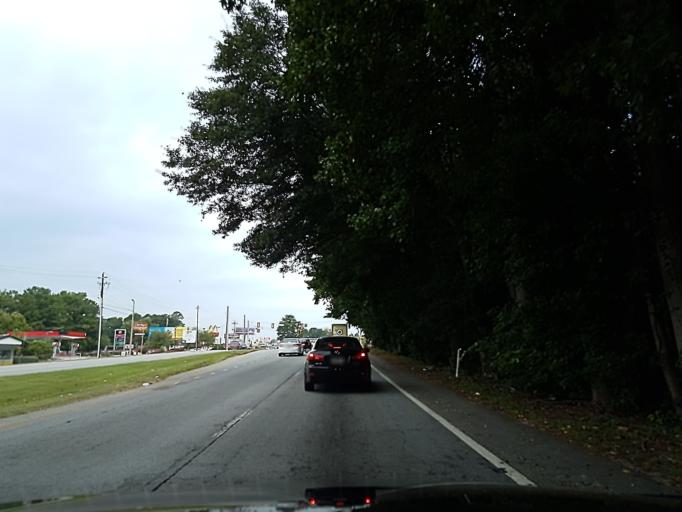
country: US
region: Georgia
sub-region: Fulton County
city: College Park
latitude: 33.6538
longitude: -84.4913
